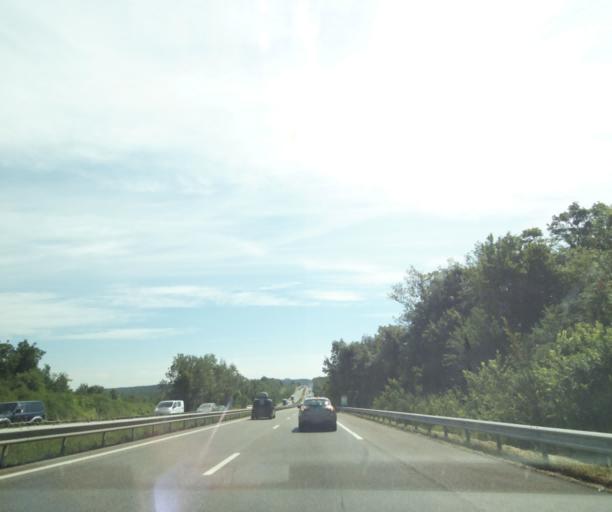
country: FR
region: Lorraine
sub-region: Departement de Meurthe-et-Moselle
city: Liverdun
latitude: 48.6931
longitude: 6.0857
